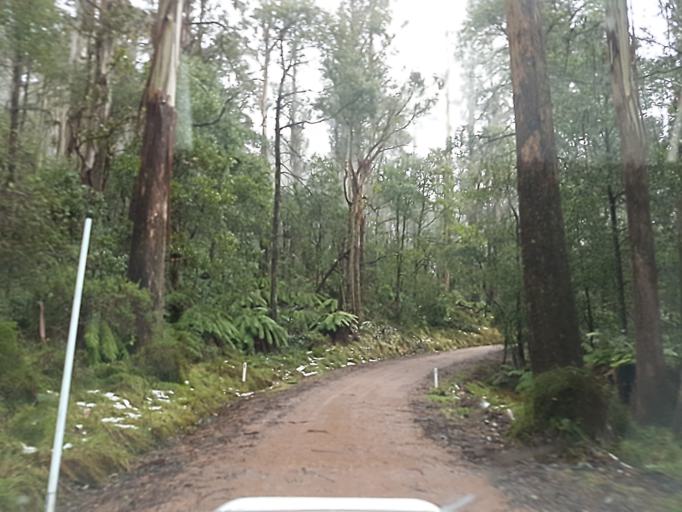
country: AU
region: Victoria
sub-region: Yarra Ranges
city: Millgrove
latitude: -37.5072
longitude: 145.9223
